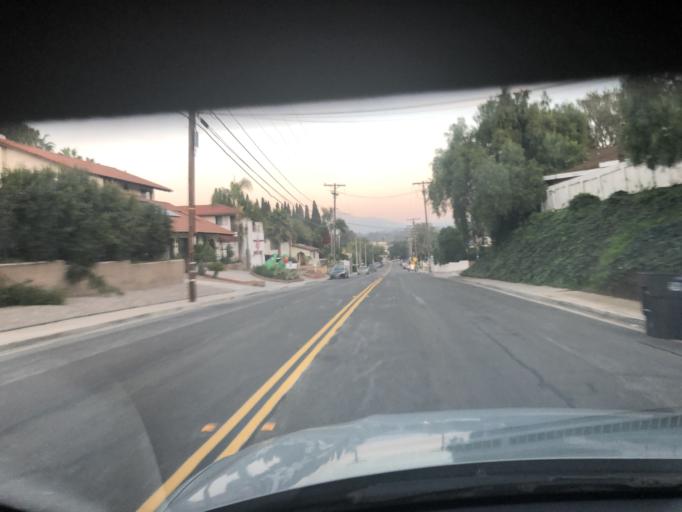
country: US
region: California
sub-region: San Diego County
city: Chula Vista
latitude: 32.6469
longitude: -117.0700
